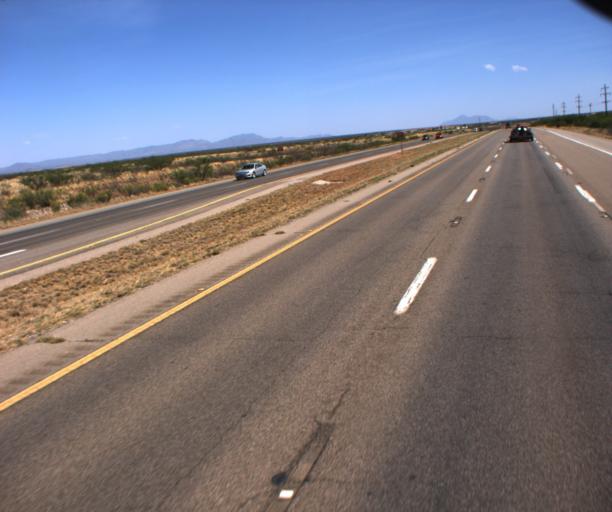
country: US
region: Arizona
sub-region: Cochise County
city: Huachuca City
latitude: 31.6557
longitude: -110.3468
